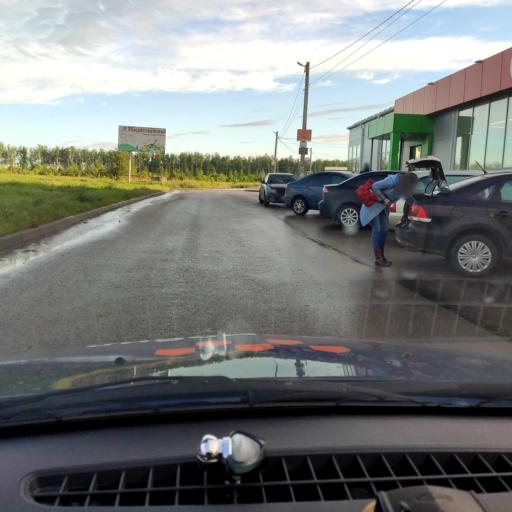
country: RU
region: Voronezj
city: Podgornoye
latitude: 51.7889
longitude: 39.1909
